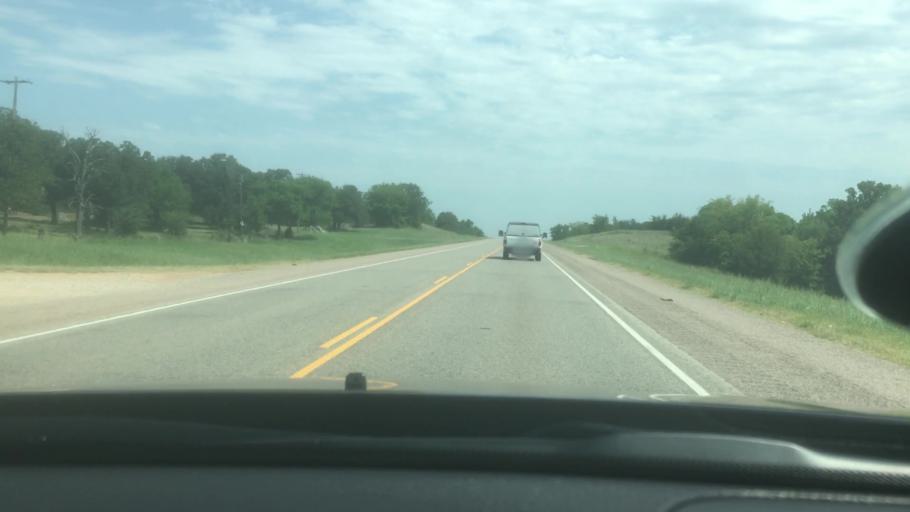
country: US
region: Oklahoma
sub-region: Seminole County
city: Maud
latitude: 35.0527
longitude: -96.9314
